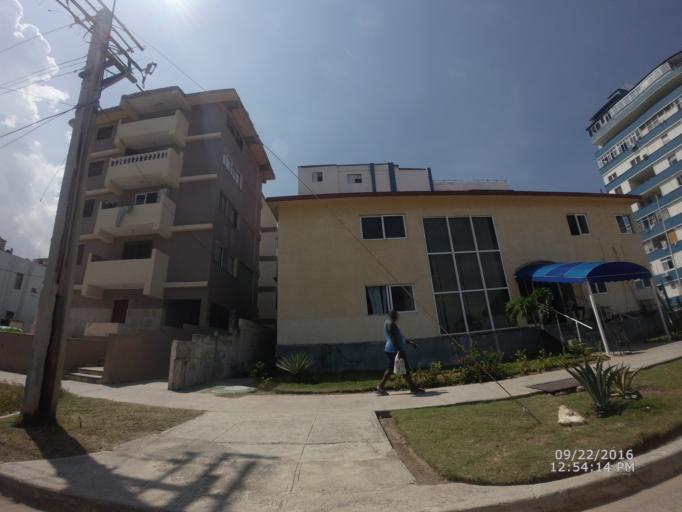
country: CU
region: La Habana
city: Havana
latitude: 23.1451
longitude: -82.3869
